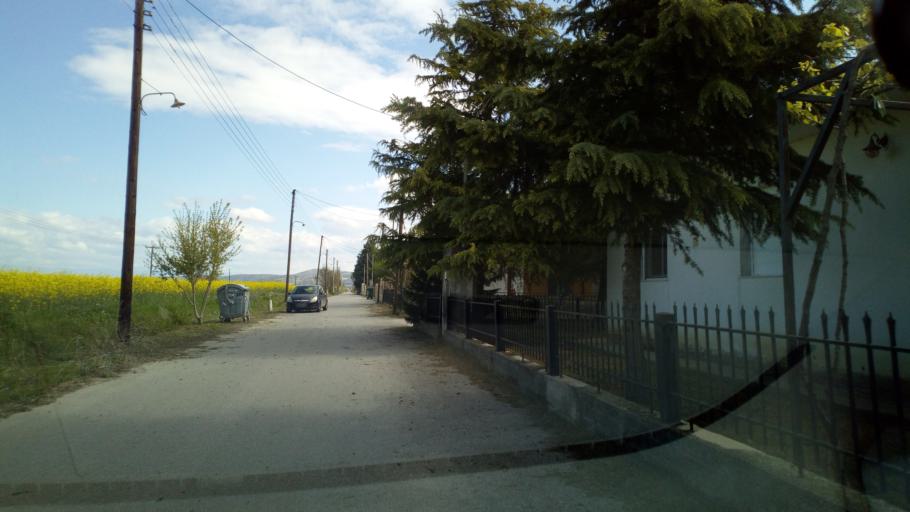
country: GR
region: Central Macedonia
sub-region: Nomos Kilkis
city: Gallikos
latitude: 40.8302
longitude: 22.8892
